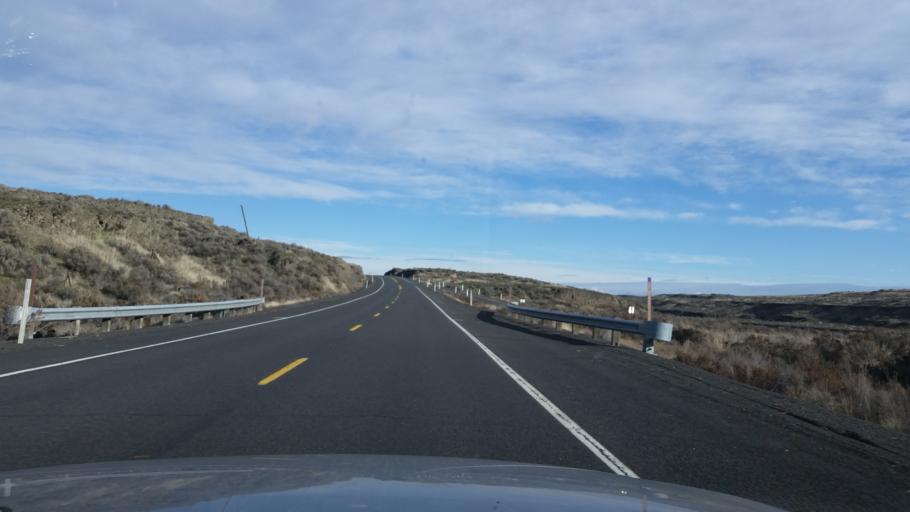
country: US
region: Washington
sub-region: Adams County
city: Ritzville
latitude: 47.3617
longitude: -118.4782
